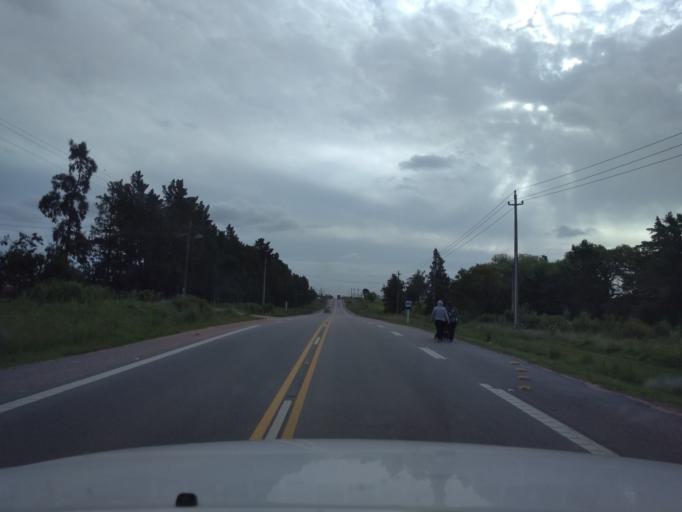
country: UY
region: Canelones
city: Joaquin Suarez
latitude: -34.7058
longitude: -56.0479
